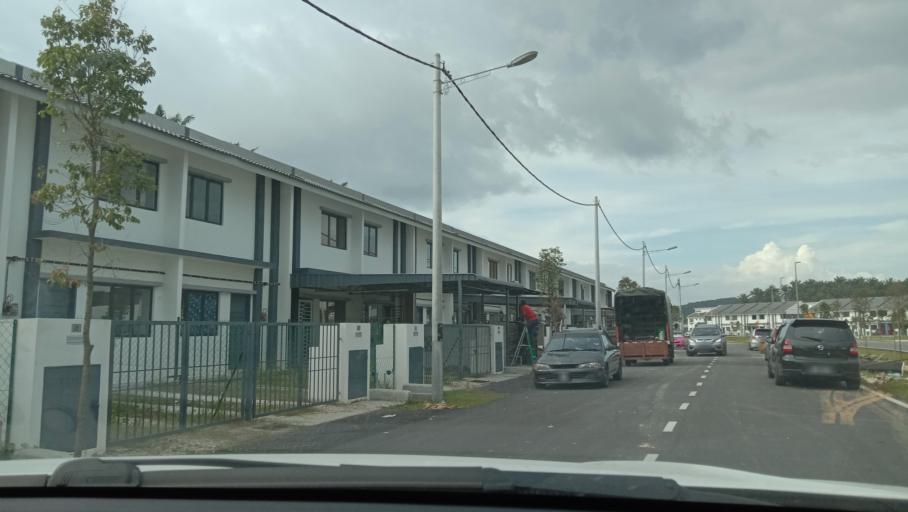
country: MY
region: Selangor
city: Ladang Seri Kundang
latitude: 3.2345
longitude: 101.4773
